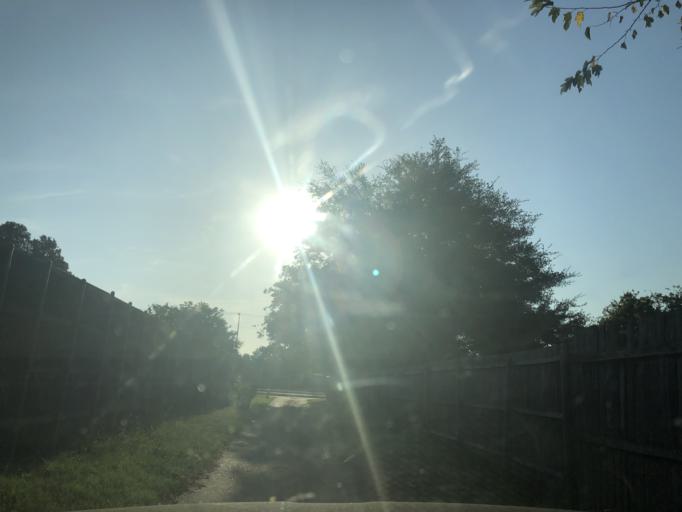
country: US
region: Texas
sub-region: Dallas County
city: Garland
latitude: 32.8507
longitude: -96.6345
